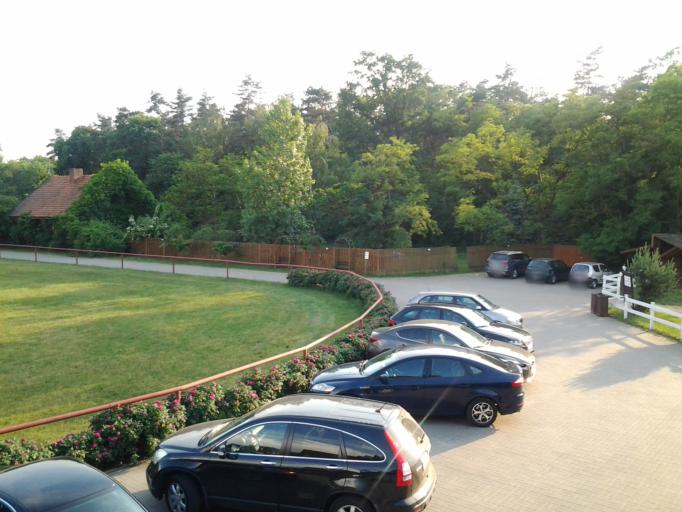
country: PL
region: Greater Poland Voivodeship
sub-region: Powiat sredzki
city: Nowe Miasto nad Warta
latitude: 52.0950
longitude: 17.4429
